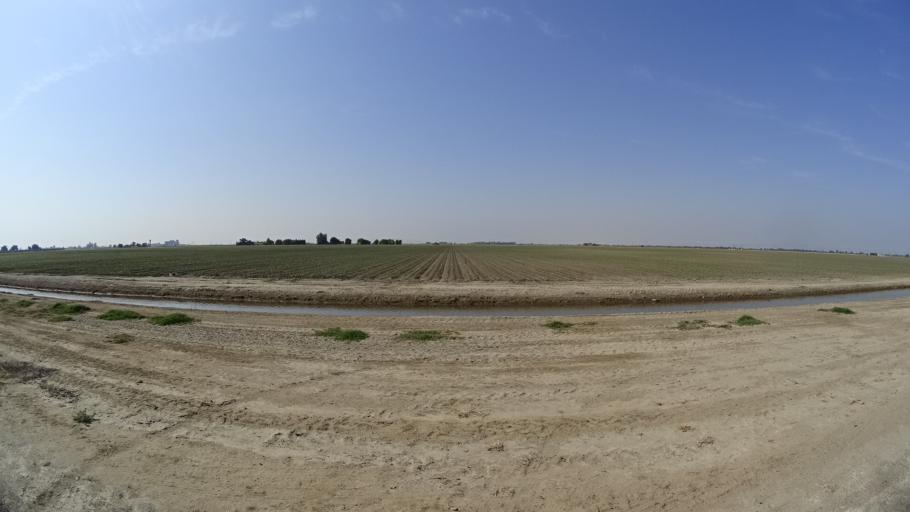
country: US
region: California
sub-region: Kings County
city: Lemoore
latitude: 36.3206
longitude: -119.8371
